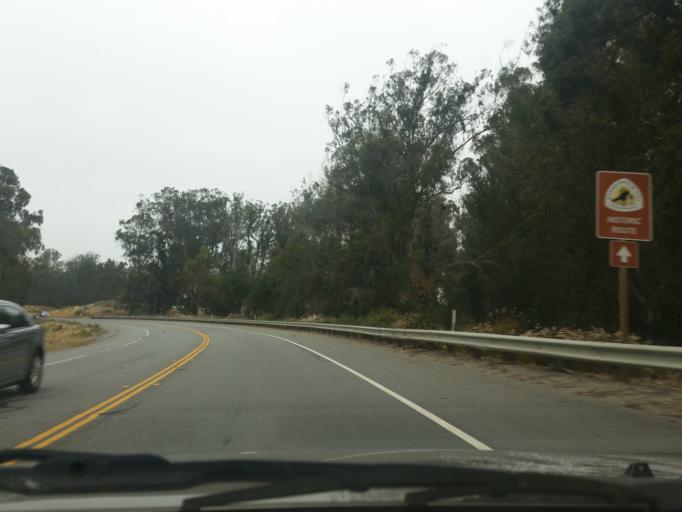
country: US
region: California
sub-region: San Luis Obispo County
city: Callender
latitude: 35.0501
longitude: -120.5929
